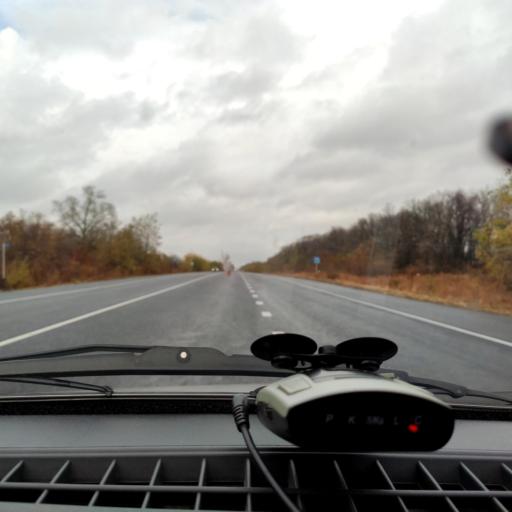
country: RU
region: Voronezj
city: Uryv-Pokrovka
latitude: 51.2330
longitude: 39.0591
